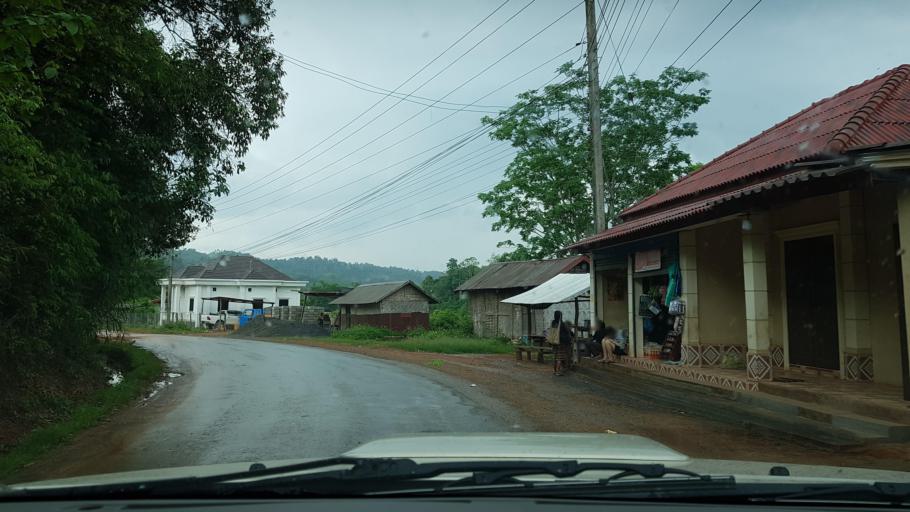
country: LA
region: Oudomxai
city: Muang Xay
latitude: 20.5754
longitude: 101.9223
